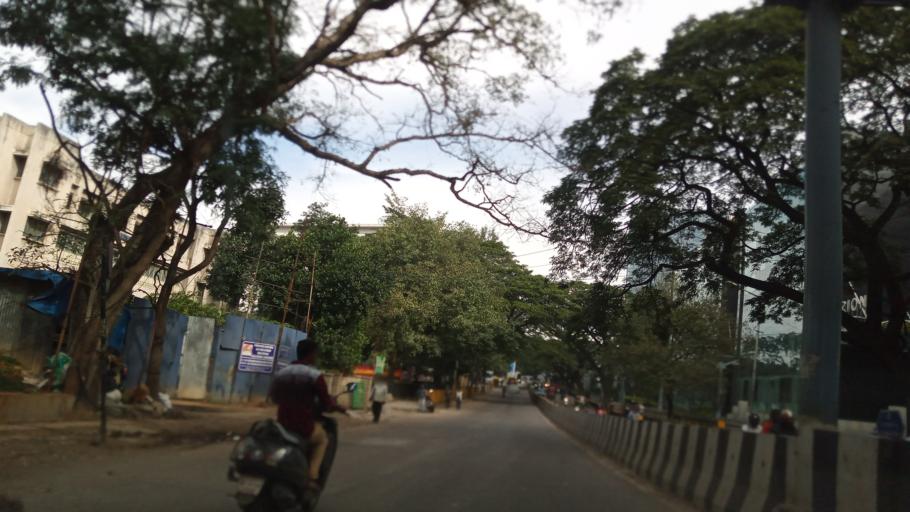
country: IN
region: Karnataka
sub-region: Bangalore Urban
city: Bangalore
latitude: 13.0104
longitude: 77.5544
